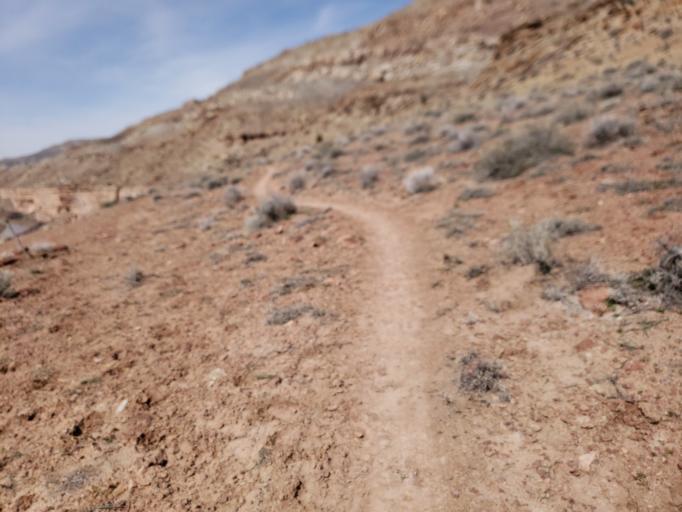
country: US
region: Colorado
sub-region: Mesa County
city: Loma
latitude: 39.1913
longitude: -108.8834
